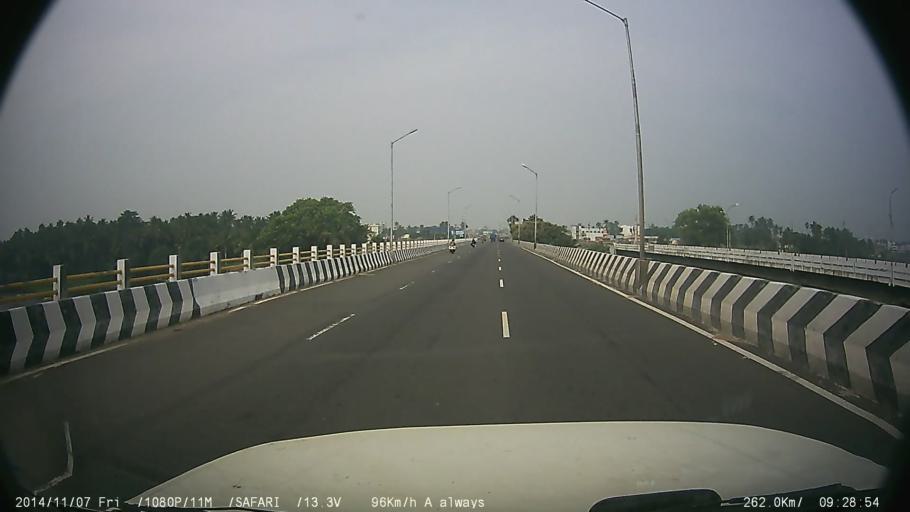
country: IN
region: Tamil Nadu
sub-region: Erode
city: Bhavani
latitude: 11.4316
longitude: 77.6838
